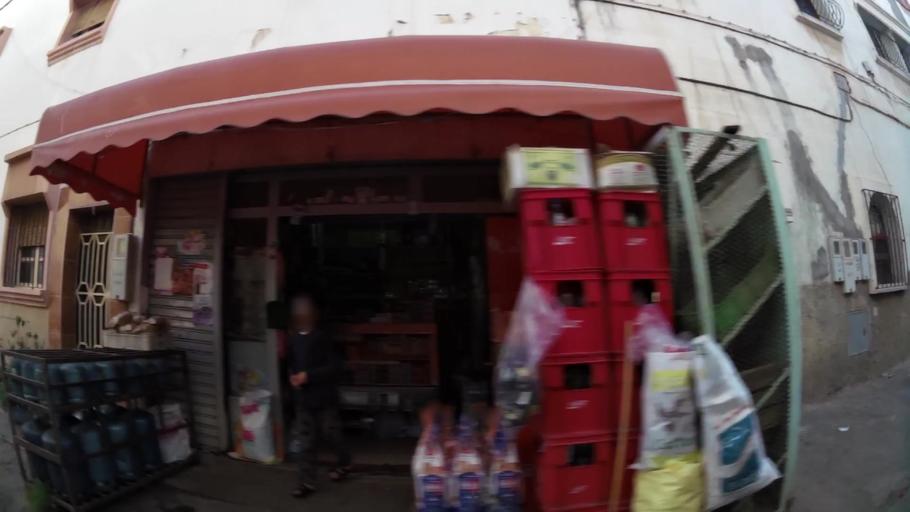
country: MA
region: Oued ed Dahab-Lagouira
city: Dakhla
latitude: 30.4123
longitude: -9.5519
